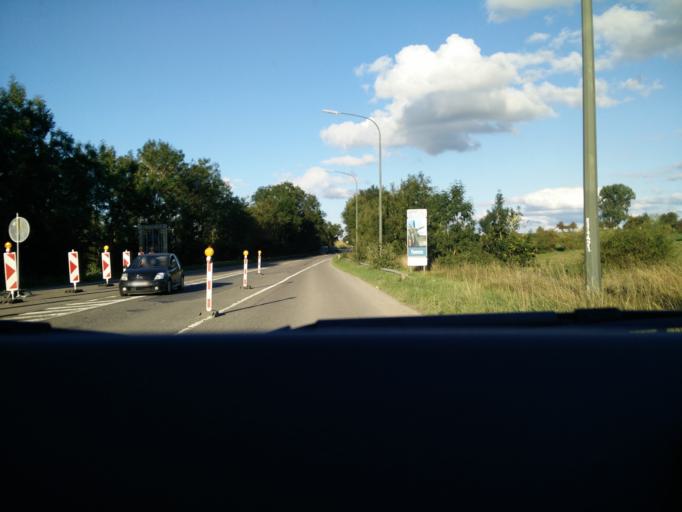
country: BE
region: Wallonia
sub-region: Province de Namur
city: Philippeville
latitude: 50.2016
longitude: 4.5643
